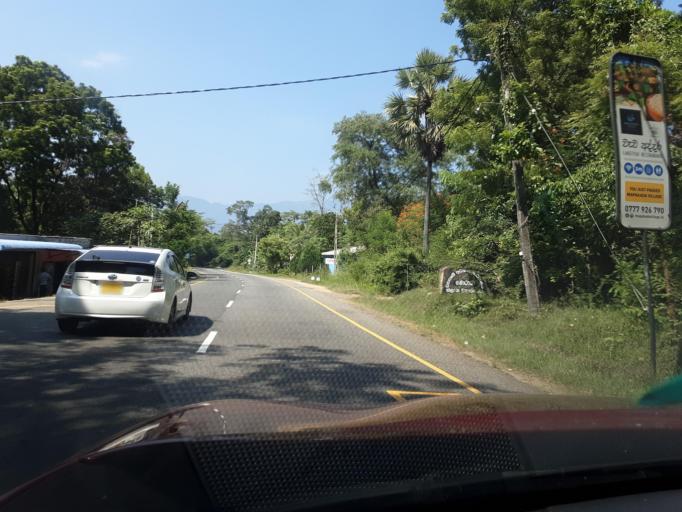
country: LK
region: Uva
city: Badulla
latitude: 7.2829
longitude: 81.0316
